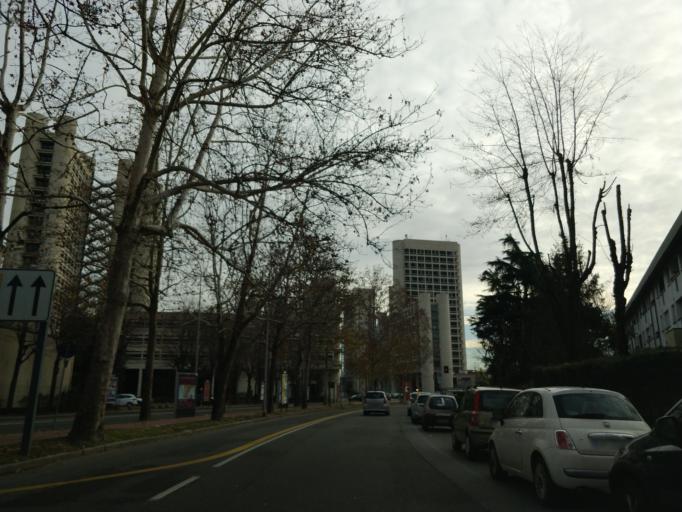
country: IT
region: Emilia-Romagna
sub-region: Provincia di Bologna
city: Bologna
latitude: 44.5100
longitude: 11.3611
